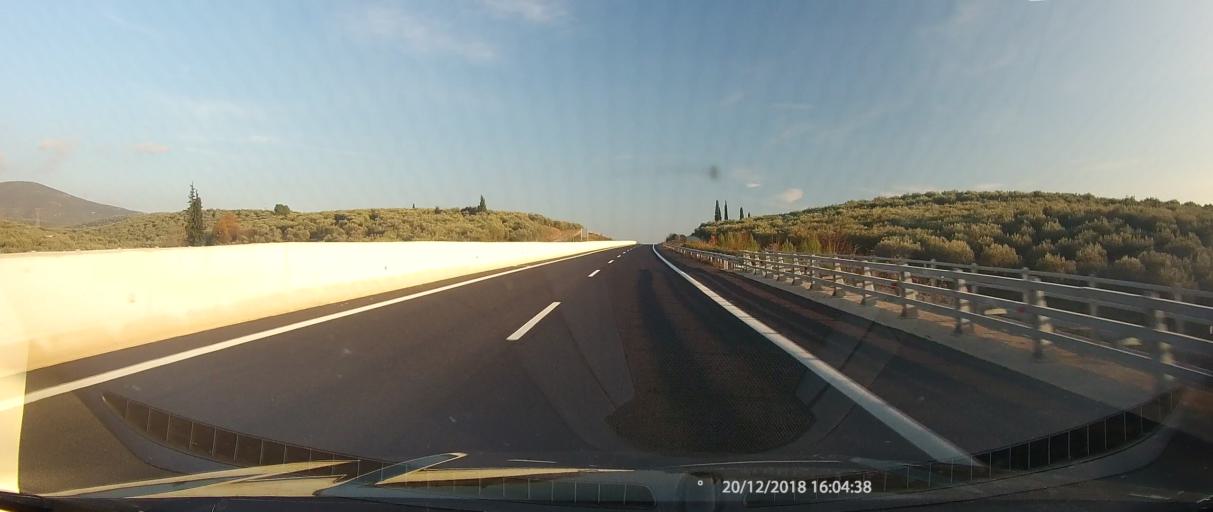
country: GR
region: Central Greece
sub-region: Nomos Fthiotidos
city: Stylida
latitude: 38.9104
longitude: 22.6671
